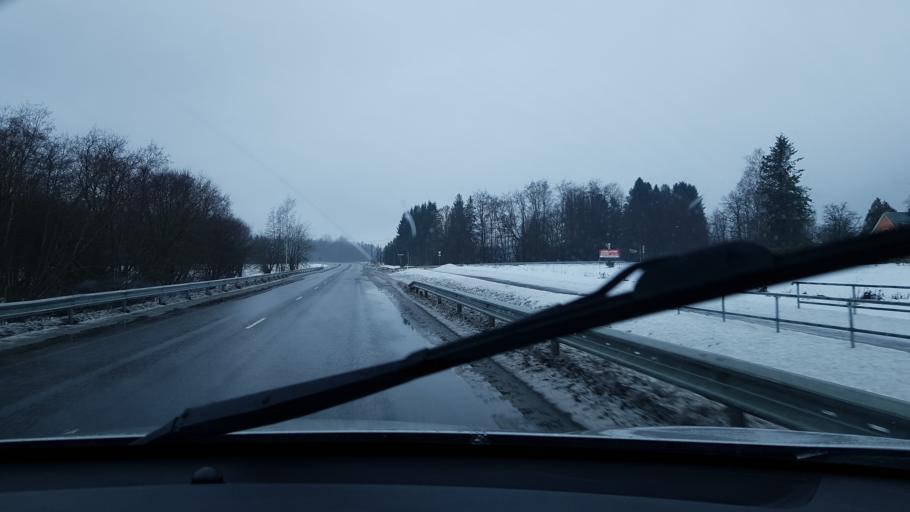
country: EE
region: Jaervamaa
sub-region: Tueri vald
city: Tueri
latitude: 58.8170
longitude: 25.3943
